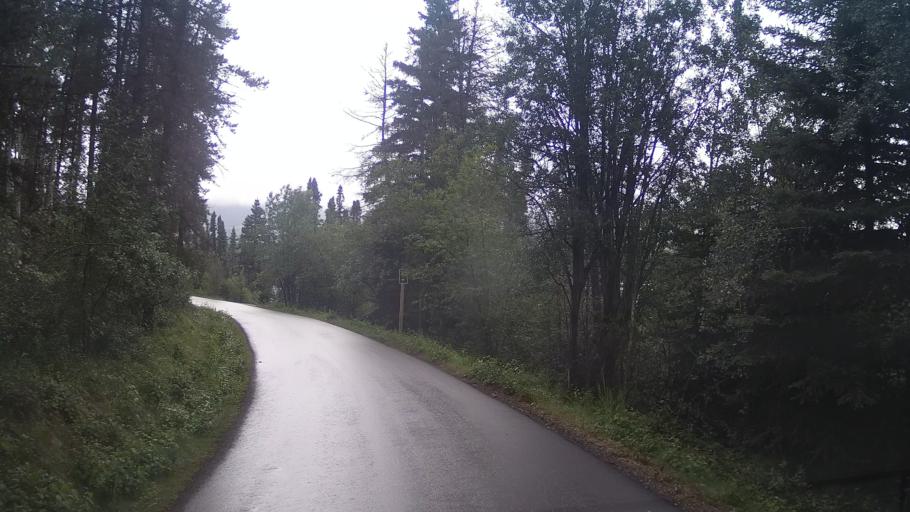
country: CA
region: Alberta
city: Jasper Park Lodge
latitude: 52.9145
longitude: -118.0977
